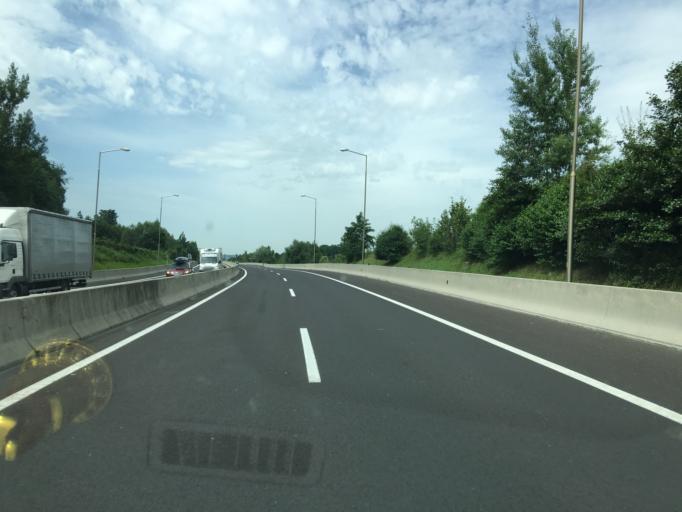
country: AT
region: Upper Austria
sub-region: Politischer Bezirk Kirchdorf an der Krems
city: Micheldorf in Oberoesterreich
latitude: 47.8920
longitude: 14.1055
